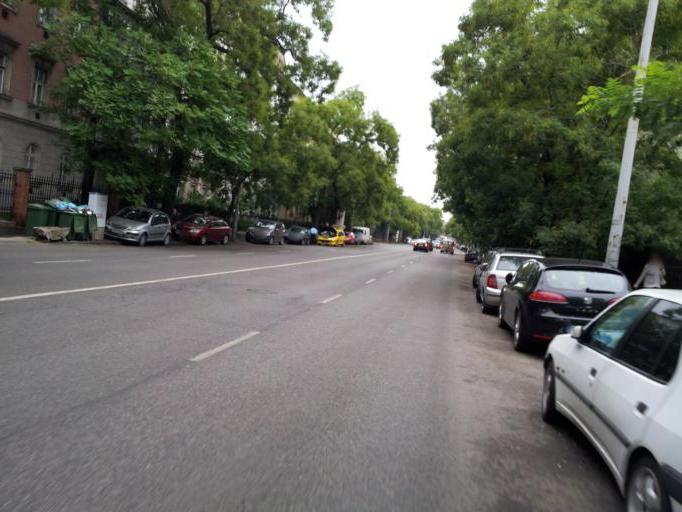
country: HU
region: Budapest
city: Budapest VII. keruelet
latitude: 47.5050
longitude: 19.0747
